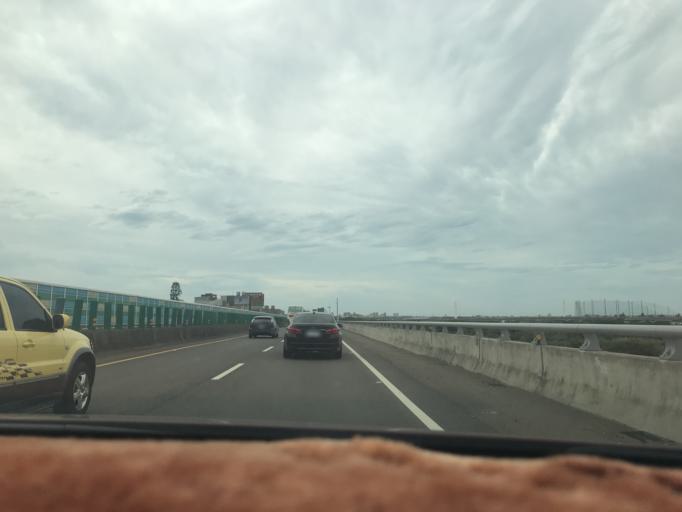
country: TW
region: Taiwan
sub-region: Hsinchu
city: Zhubei
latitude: 24.8221
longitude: 120.9877
